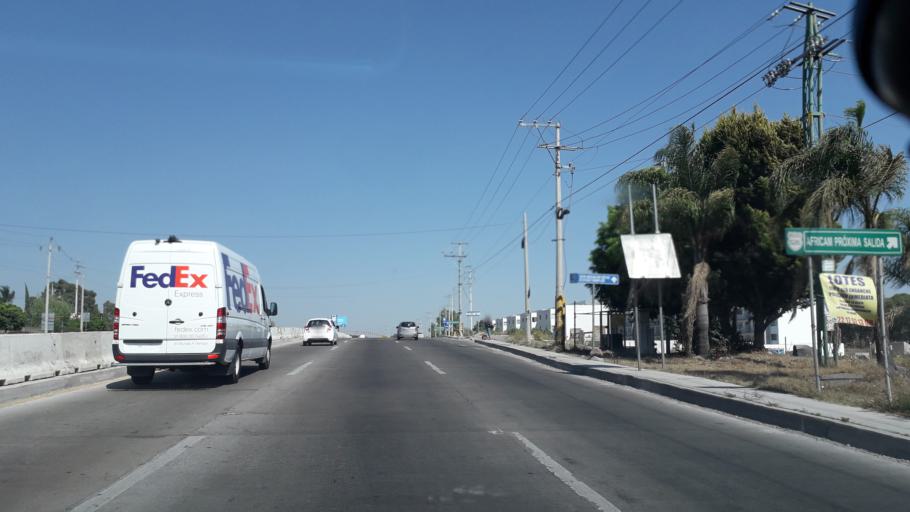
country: MX
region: Puebla
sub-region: Puebla
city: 18 de Marzo
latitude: 18.9719
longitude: -98.2042
